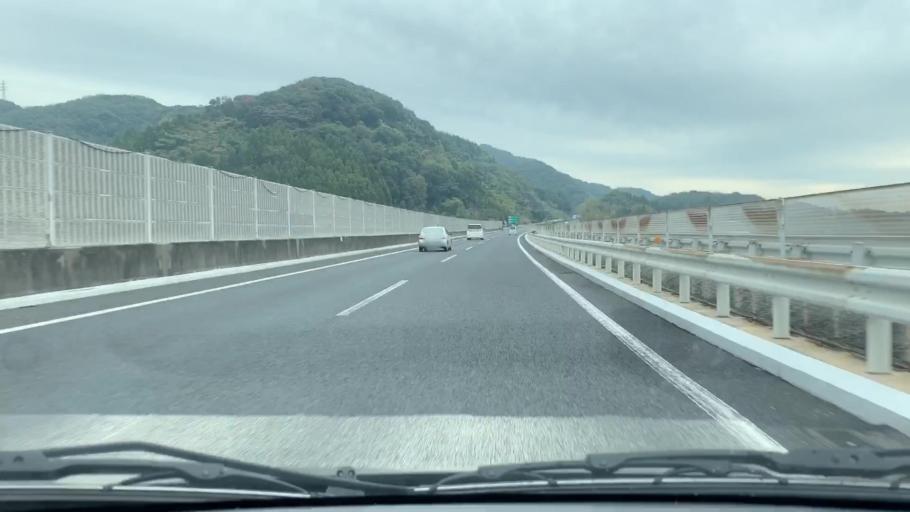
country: JP
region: Saga Prefecture
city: Saga-shi
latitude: 33.2964
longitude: 130.1733
